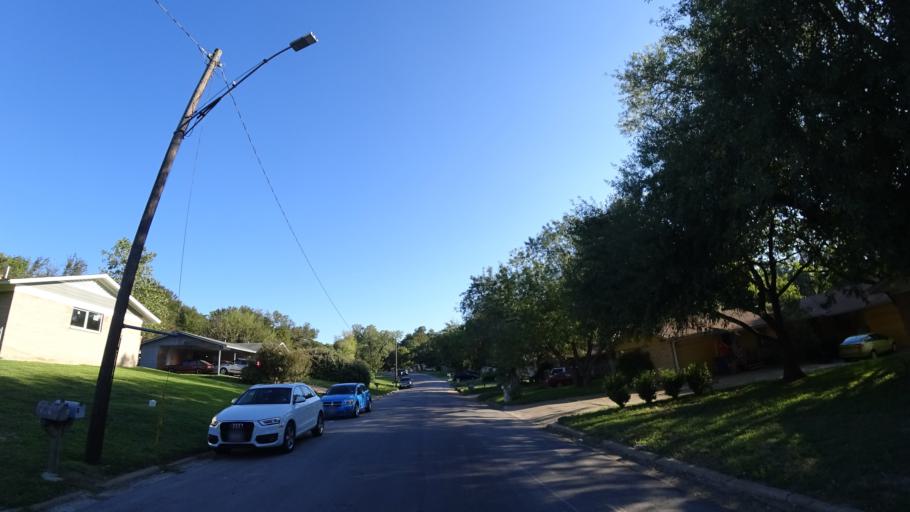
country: US
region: Texas
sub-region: Travis County
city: Austin
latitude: 30.2218
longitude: -97.7356
